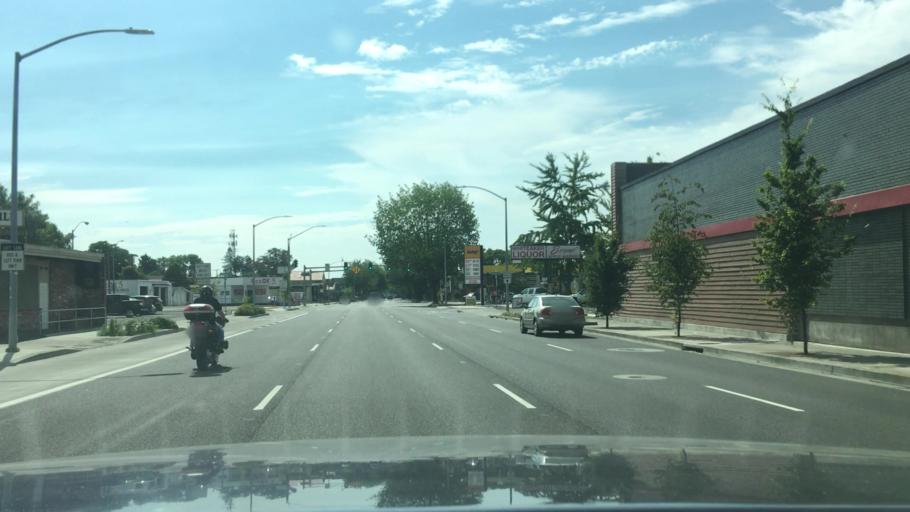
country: US
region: Oregon
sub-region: Lane County
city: Eugene
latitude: 44.0533
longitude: -123.1053
